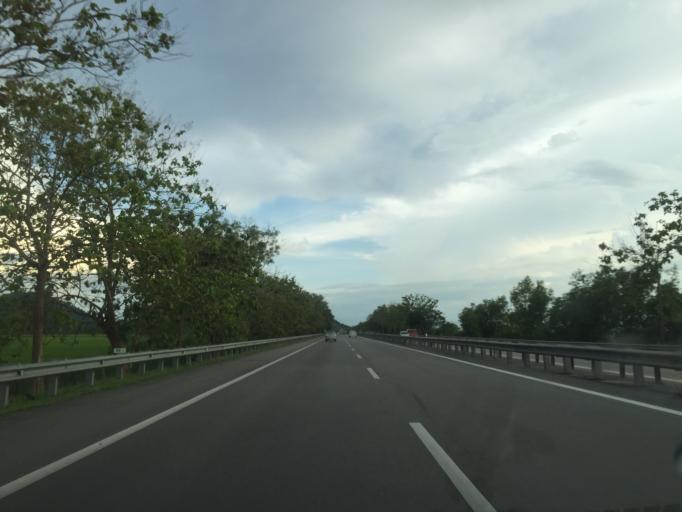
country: MY
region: Kedah
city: Gurun
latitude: 5.9576
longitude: 100.4495
